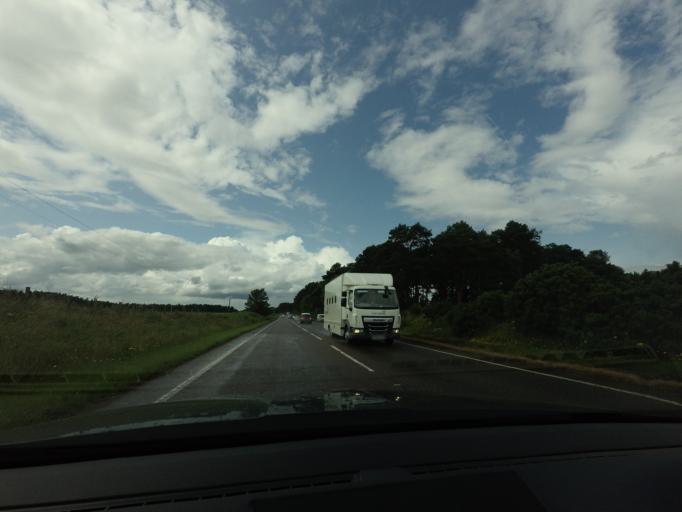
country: GB
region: Scotland
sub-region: Moray
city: Lhanbryd
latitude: 57.6313
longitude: -3.1780
